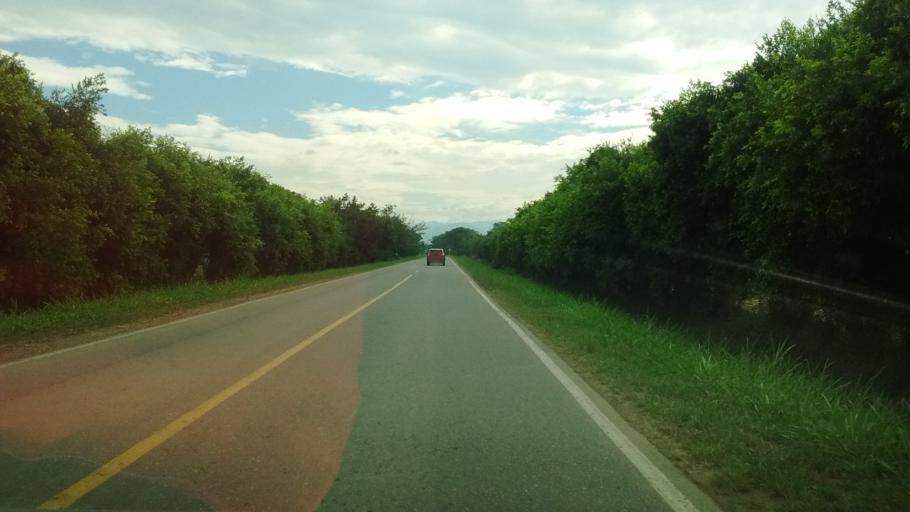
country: CO
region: Cauca
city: Santander de Quilichao
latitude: 3.0432
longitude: -76.4551
